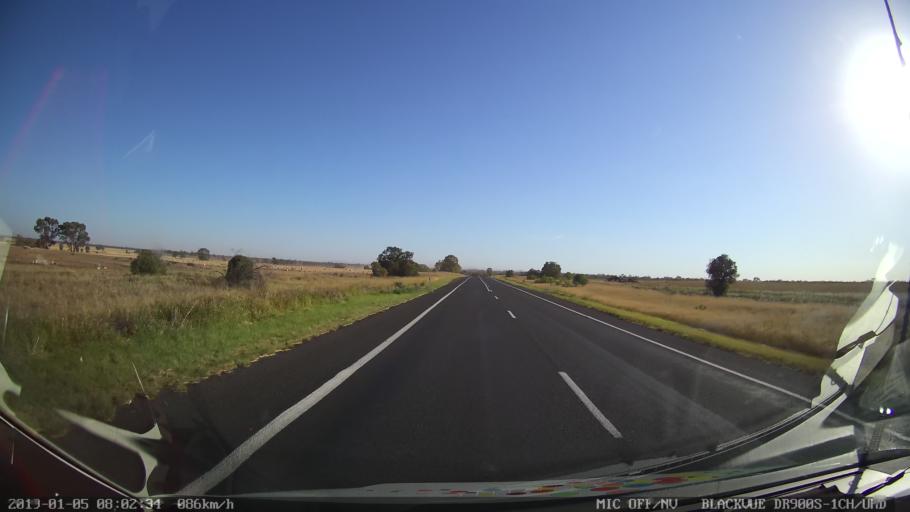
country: AU
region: New South Wales
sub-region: Gilgandra
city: Gilgandra
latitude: -31.6747
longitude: 148.7124
